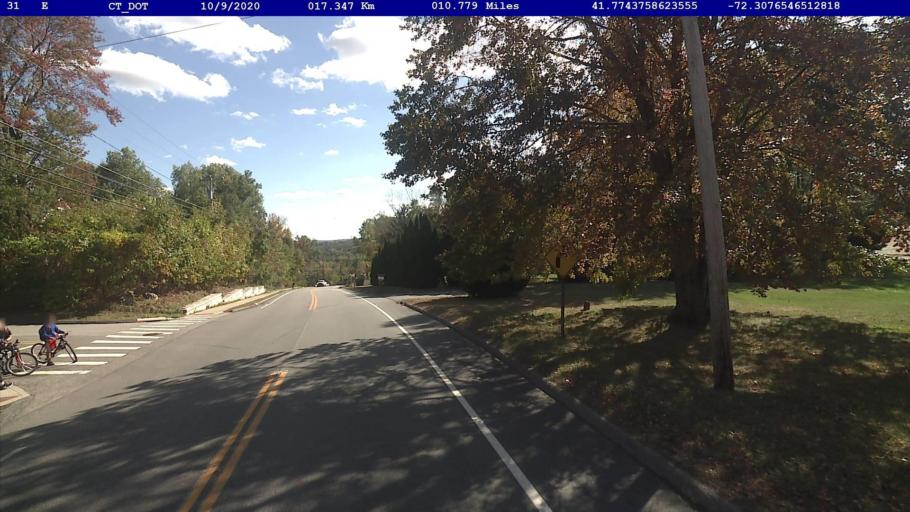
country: US
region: Connecticut
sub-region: Tolland County
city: South Coventry
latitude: 41.7744
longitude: -72.3077
